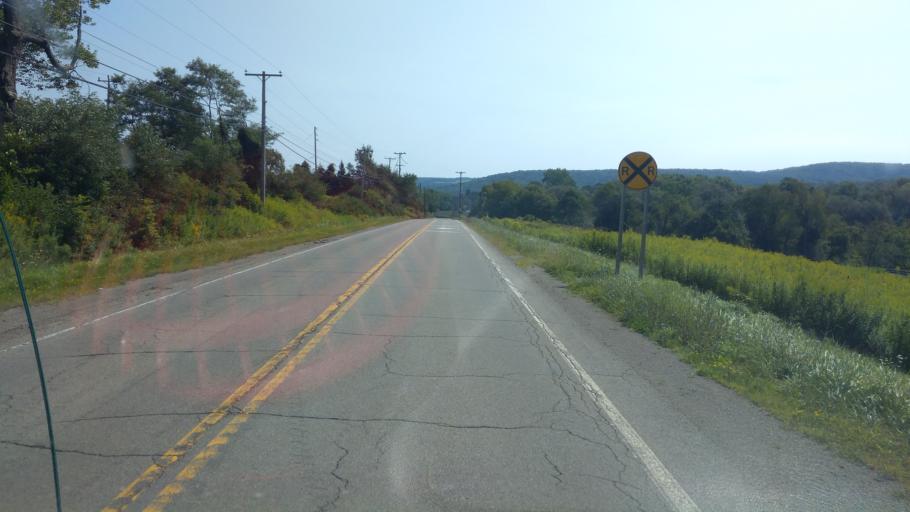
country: US
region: New York
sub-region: Allegany County
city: Friendship
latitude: 42.2007
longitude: -78.1652
